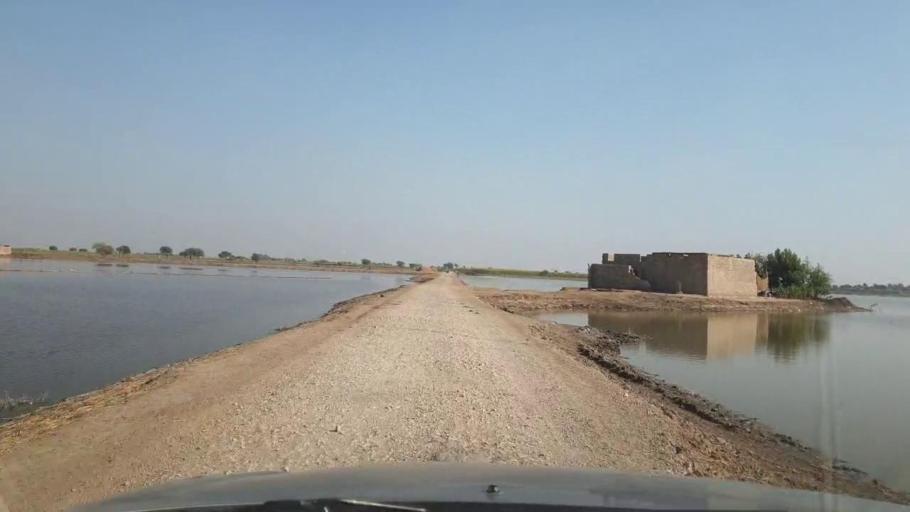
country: PK
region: Sindh
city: Tando Muhammad Khan
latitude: 25.1143
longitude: 68.5922
